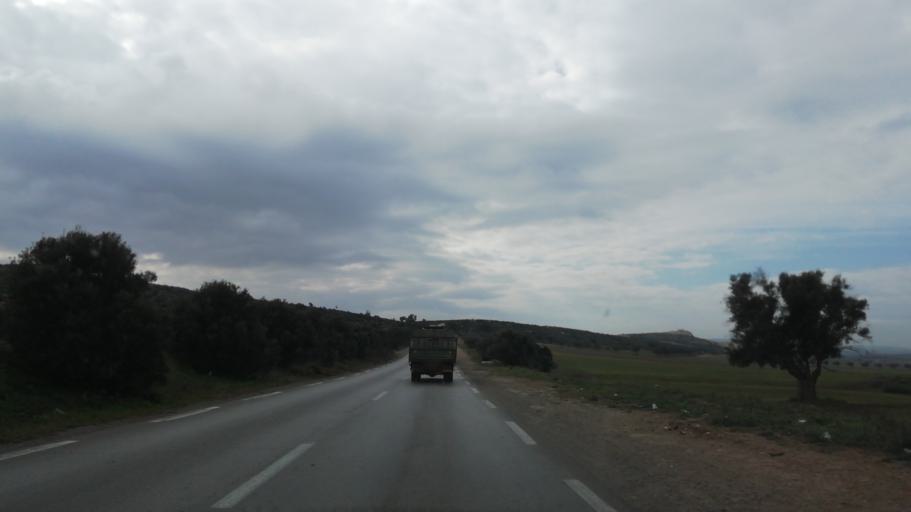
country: DZ
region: Oran
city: Ain el Bya
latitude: 35.7236
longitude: -0.3565
